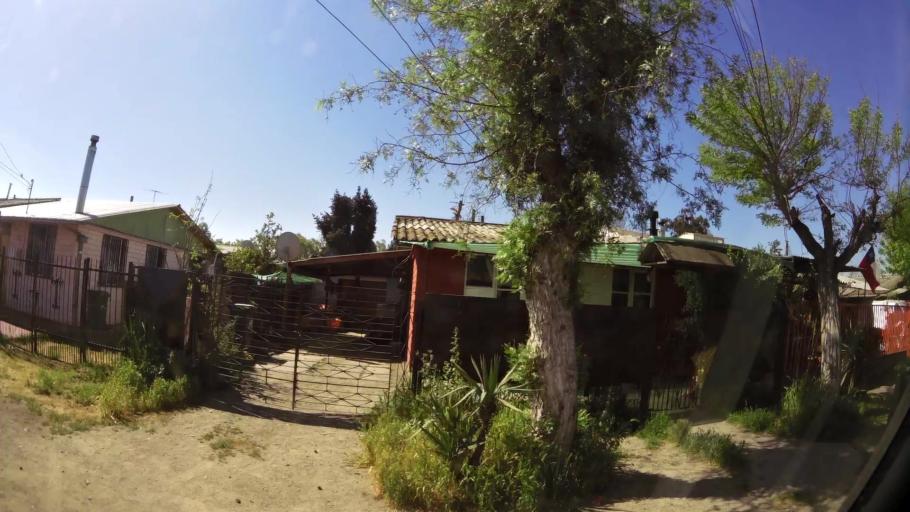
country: CL
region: Santiago Metropolitan
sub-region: Provincia de Talagante
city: Penaflor
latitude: -33.6019
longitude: -70.8906
